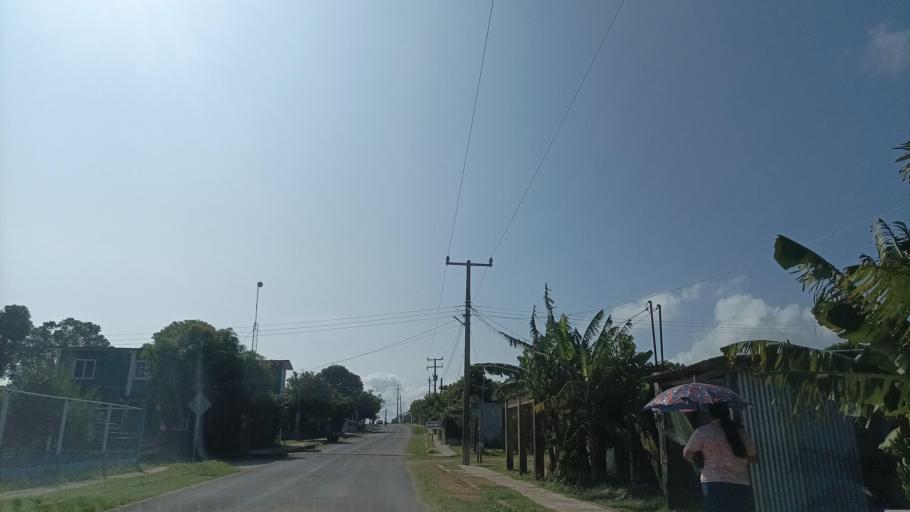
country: MX
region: Veracruz
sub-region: Coatzacoalcos
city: Fraccionamiento Ciudad Olmeca
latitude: 18.2161
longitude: -94.6142
